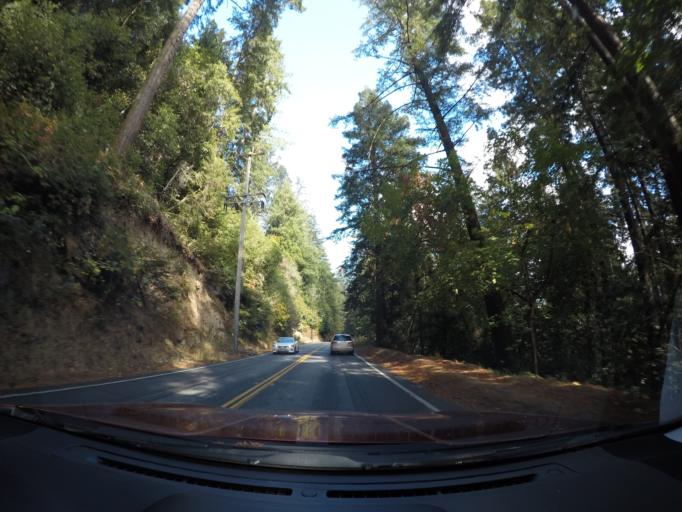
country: US
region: California
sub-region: Santa Cruz County
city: Ben Lomond
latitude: 37.0750
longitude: -122.0844
